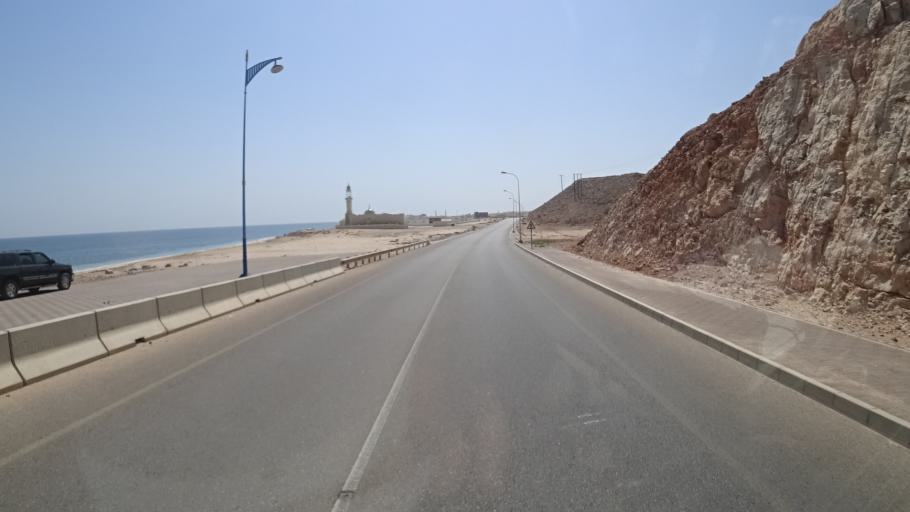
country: OM
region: Ash Sharqiyah
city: Sur
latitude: 22.5659
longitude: 59.5723
